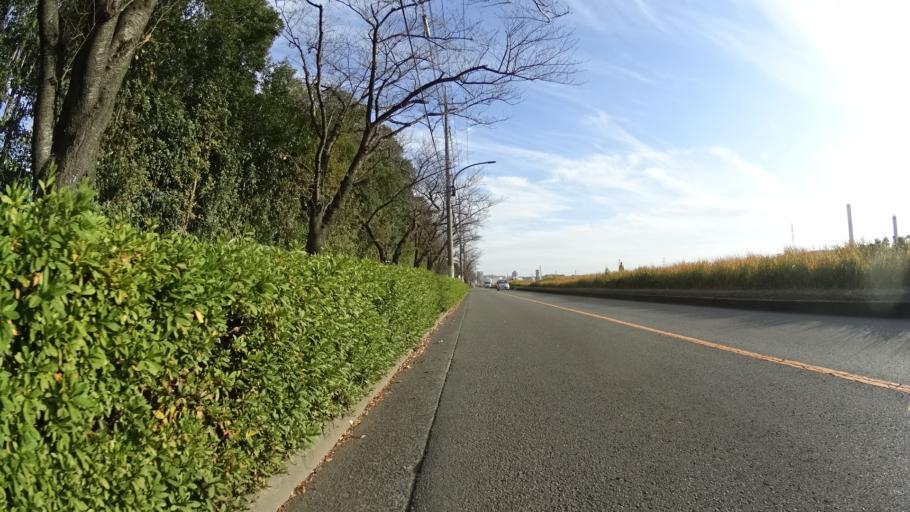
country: JP
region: Tokyo
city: Hino
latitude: 35.6712
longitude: 139.4310
